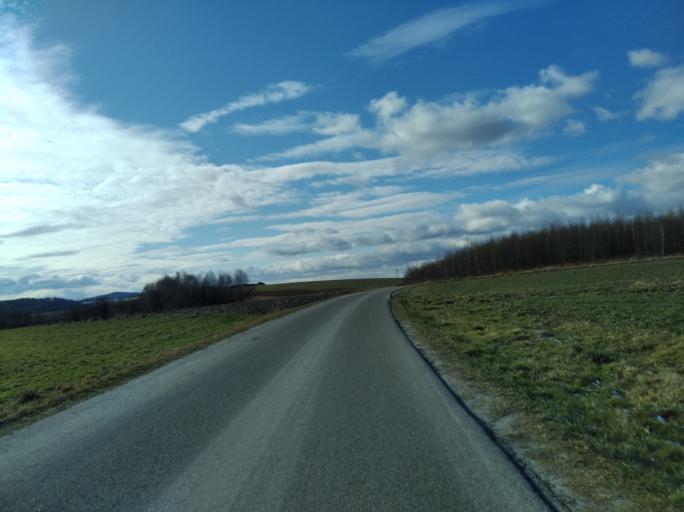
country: PL
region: Subcarpathian Voivodeship
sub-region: Powiat ropczycko-sedziszowski
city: Wielopole Skrzynskie
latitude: 49.9167
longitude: 21.6270
